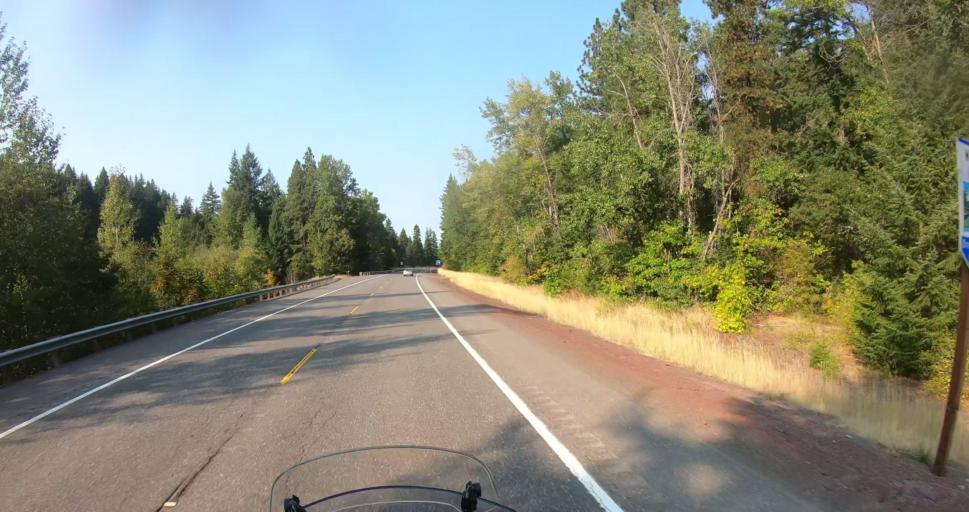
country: US
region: Oregon
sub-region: Hood River County
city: Odell
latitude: 45.4914
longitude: -121.5627
